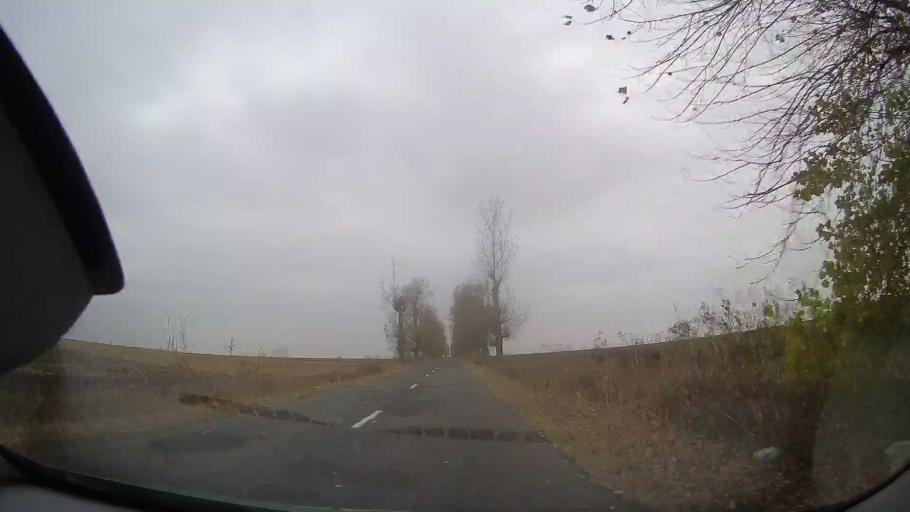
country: RO
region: Ialomita
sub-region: Comuna Grindu
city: Grindu
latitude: 44.7686
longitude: 26.8833
